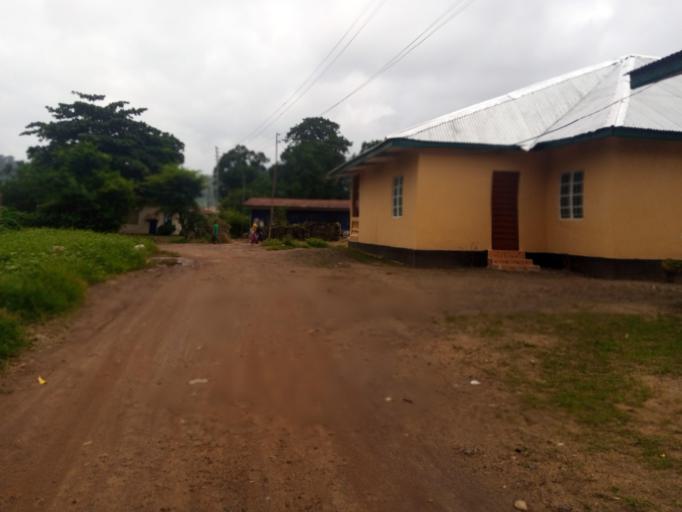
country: SL
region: Eastern Province
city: Kenema
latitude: 7.8625
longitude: -11.1964
